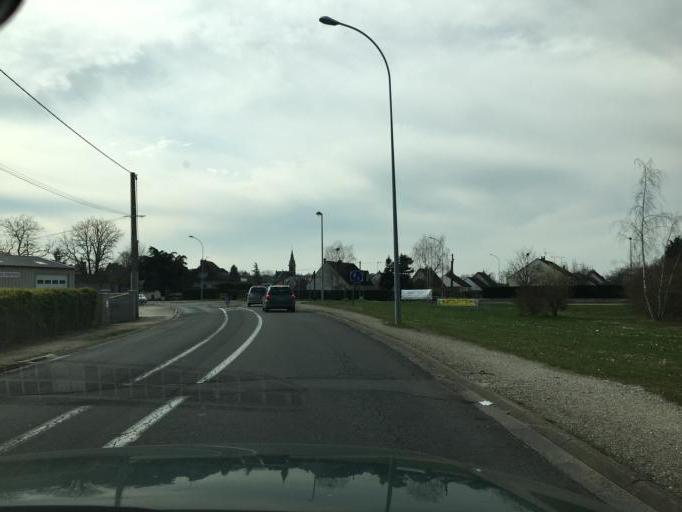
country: FR
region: Centre
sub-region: Departement du Loiret
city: Vienne-en-Val
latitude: 47.8018
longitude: 2.1412
